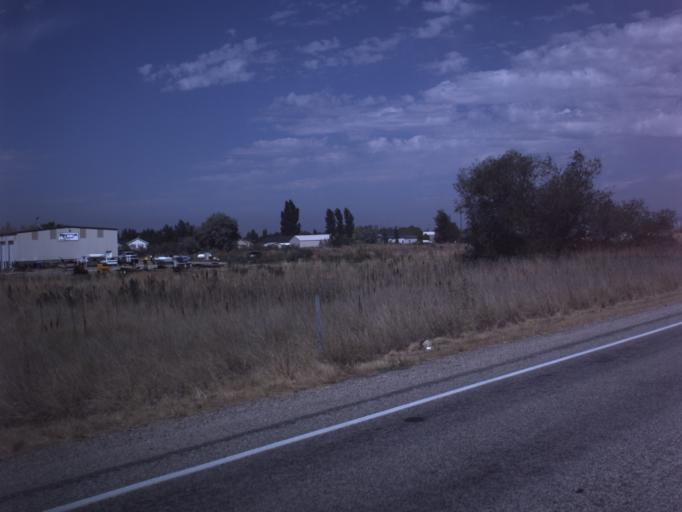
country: US
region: Utah
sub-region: Weber County
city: Farr West
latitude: 41.3272
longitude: -112.0328
